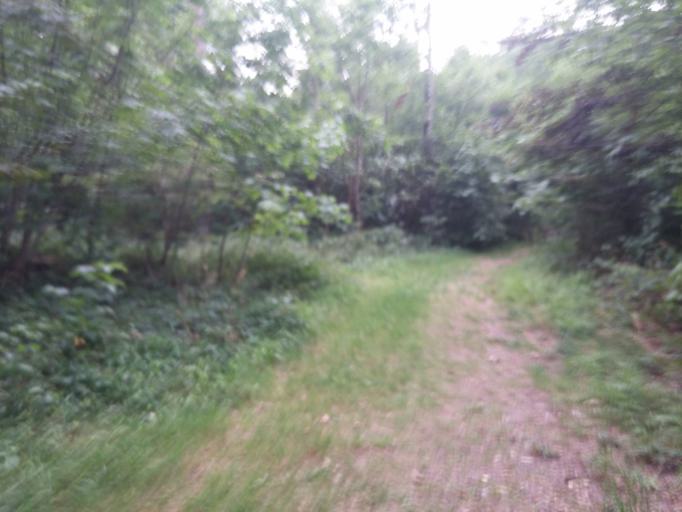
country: DE
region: Bavaria
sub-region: Upper Bavaria
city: Haar
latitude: 48.1111
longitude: 11.7363
